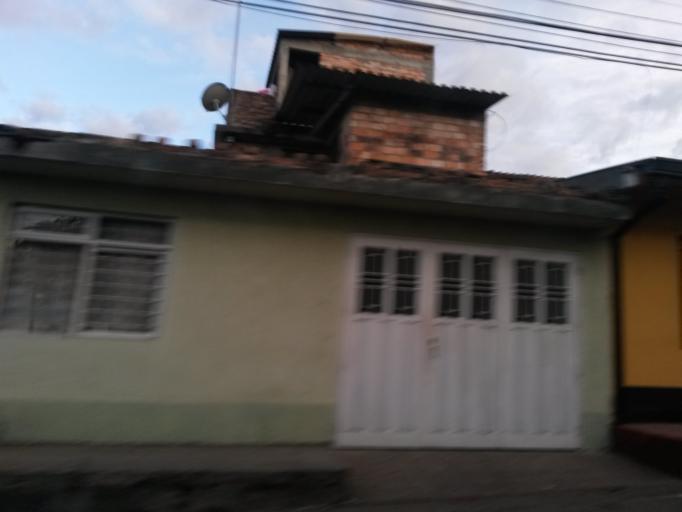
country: CO
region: Cauca
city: Popayan
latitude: 2.4586
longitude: -76.6340
